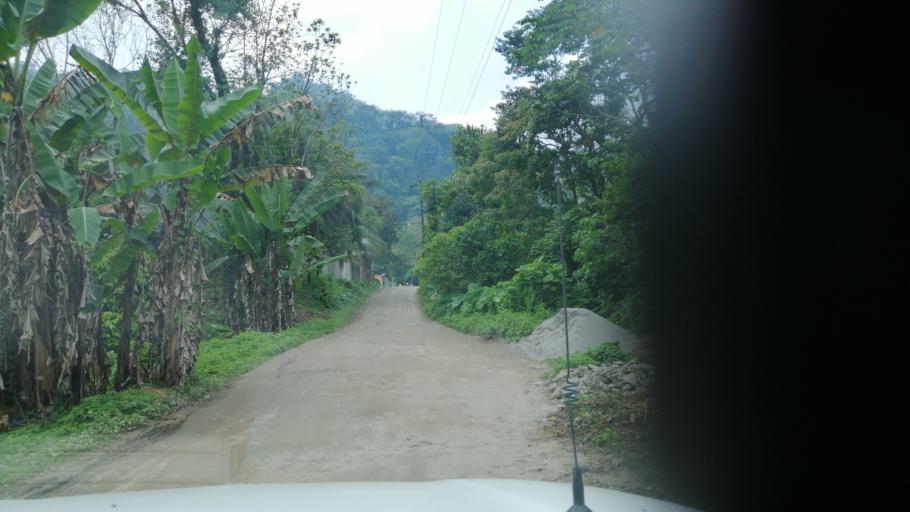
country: MX
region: Chiapas
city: Ostuacan
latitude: 17.3970
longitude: -93.3281
